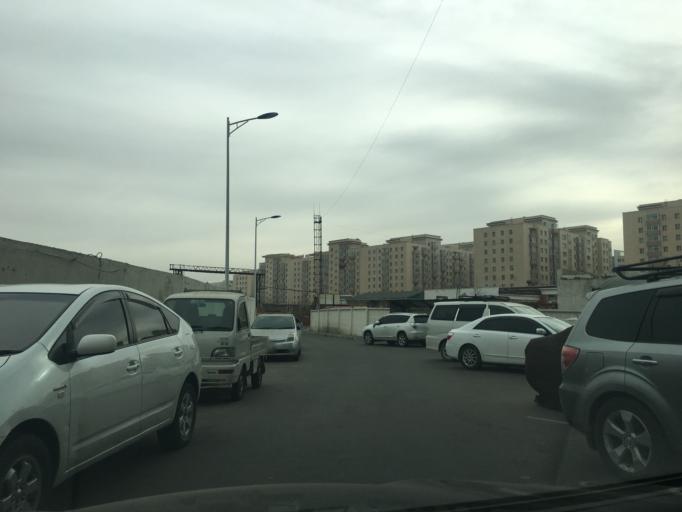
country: MN
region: Ulaanbaatar
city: Ulaanbaatar
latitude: 47.9053
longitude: 106.8870
